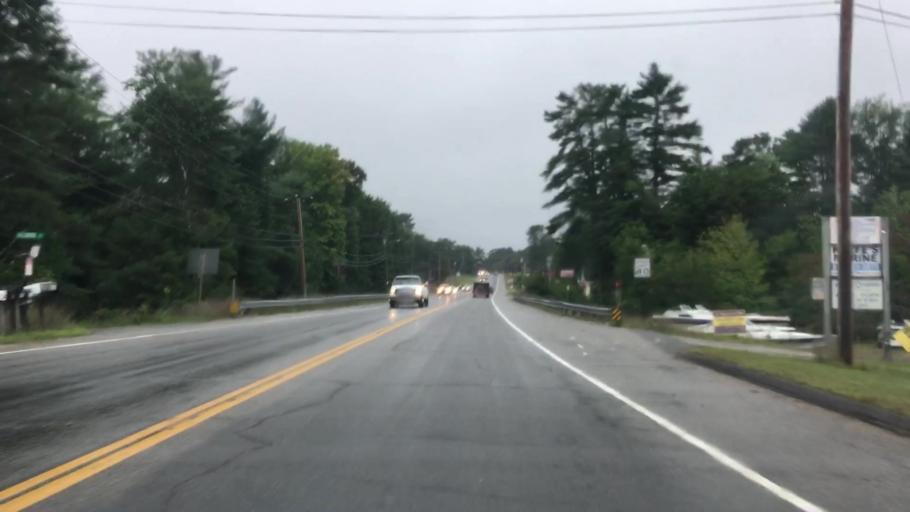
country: US
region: Maine
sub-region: Cumberland County
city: Raymond
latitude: 43.9653
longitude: -70.5788
